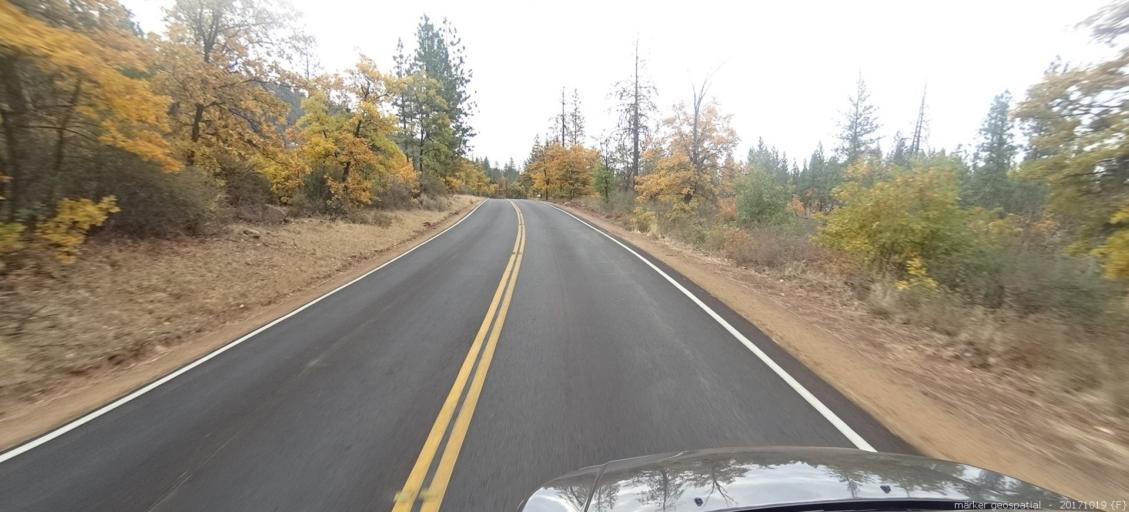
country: US
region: California
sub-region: Shasta County
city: Burney
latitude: 41.1591
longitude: -121.3562
